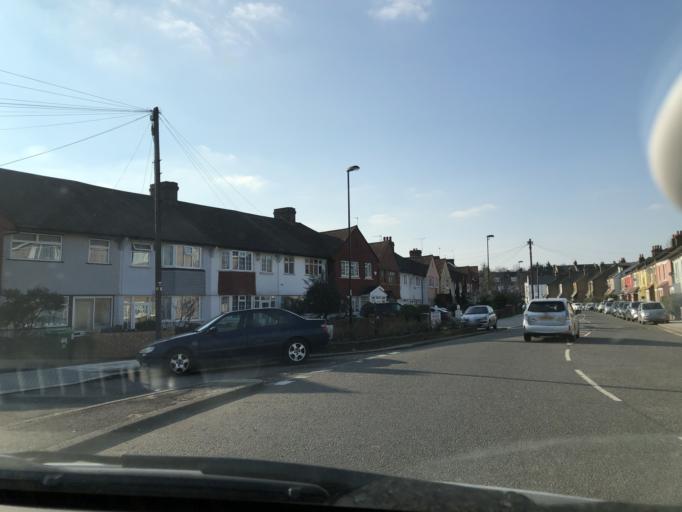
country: GB
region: England
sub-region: Greater London
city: Catford
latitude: 51.4534
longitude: -0.0346
